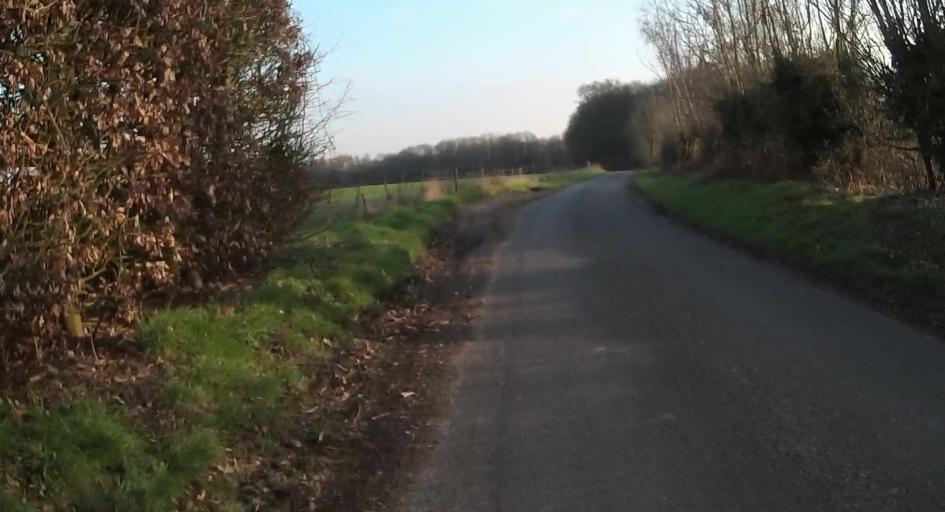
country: GB
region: England
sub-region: Hampshire
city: Alton
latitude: 51.1625
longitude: -0.9990
